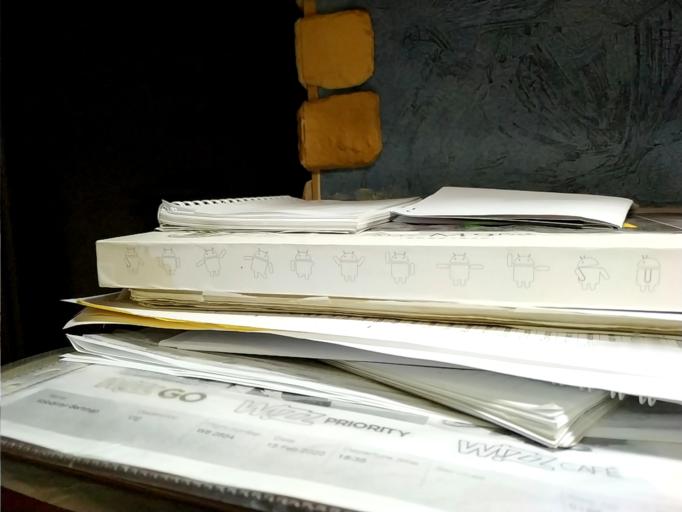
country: RU
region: Arkhangelskaya
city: Onega
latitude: 63.3036
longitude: 38.2613
